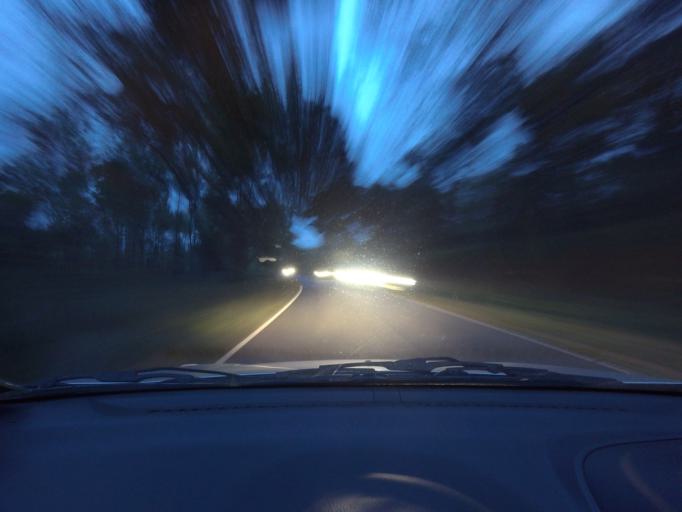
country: IN
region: Karnataka
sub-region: Hassan
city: Sakleshpur
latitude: 12.9962
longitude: 75.7039
